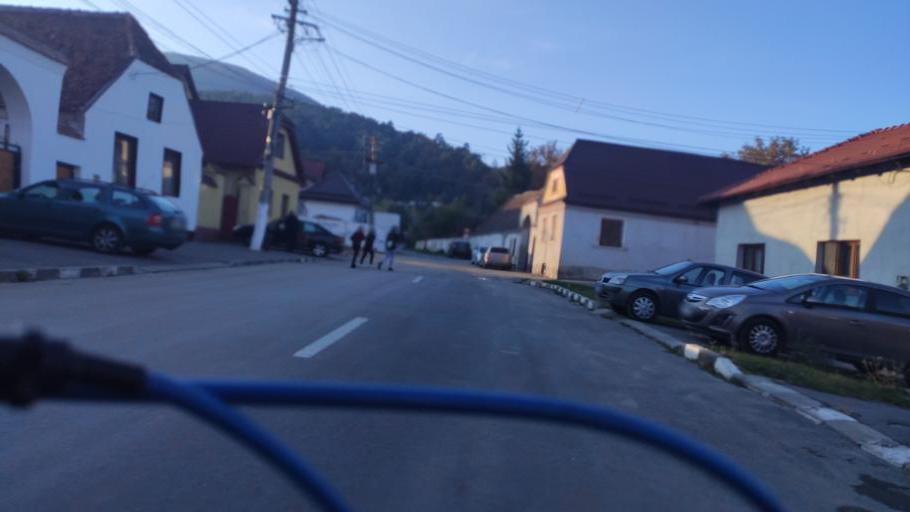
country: RO
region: Brasov
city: Codlea
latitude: 45.6999
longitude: 25.4421
